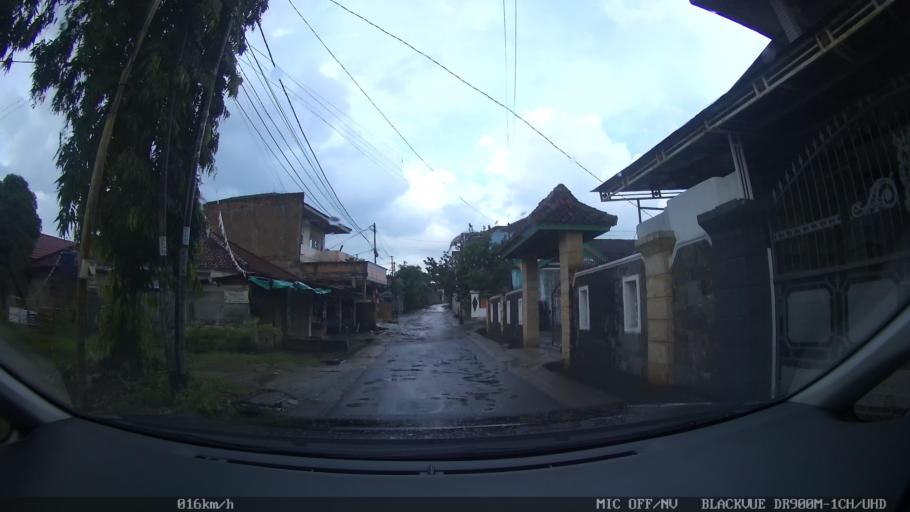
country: ID
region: Lampung
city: Kedaton
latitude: -5.3954
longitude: 105.2902
